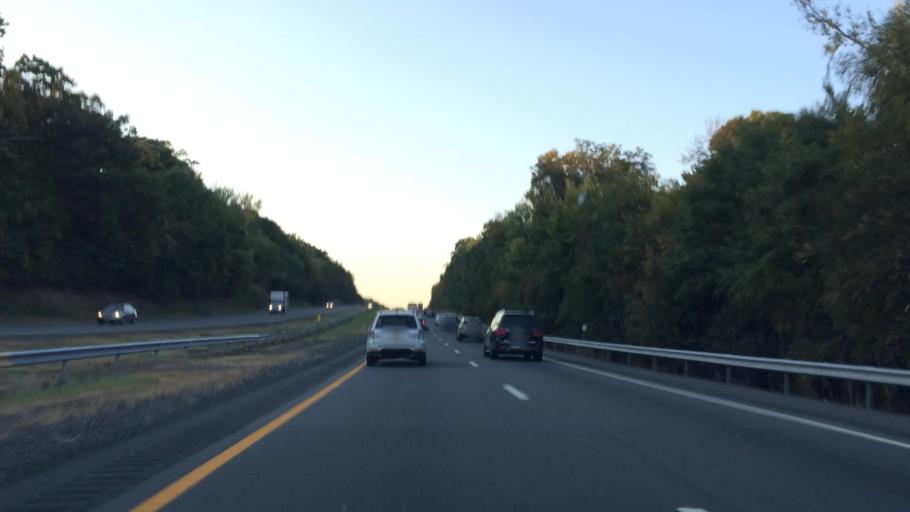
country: US
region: New York
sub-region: Orange County
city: Vails Gate
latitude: 41.4583
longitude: -74.0657
